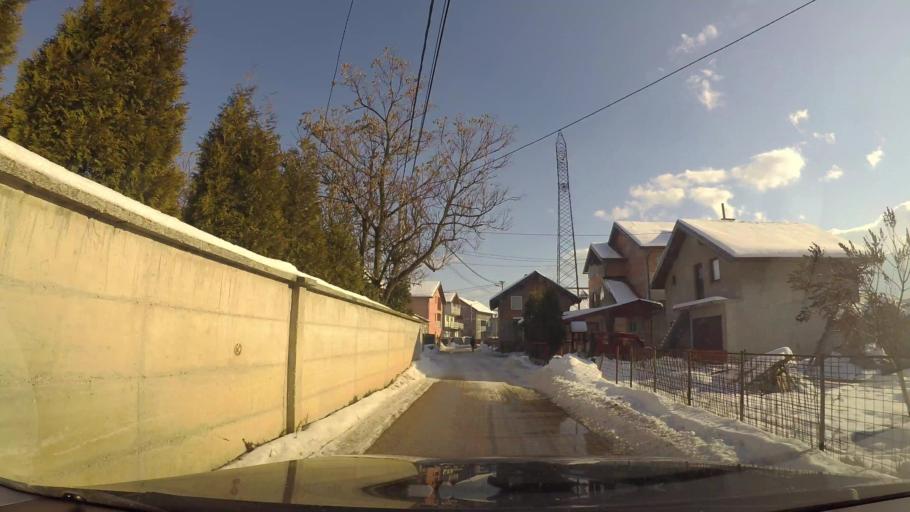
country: BA
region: Federation of Bosnia and Herzegovina
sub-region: Kanton Sarajevo
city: Sarajevo
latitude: 43.8070
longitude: 18.3301
